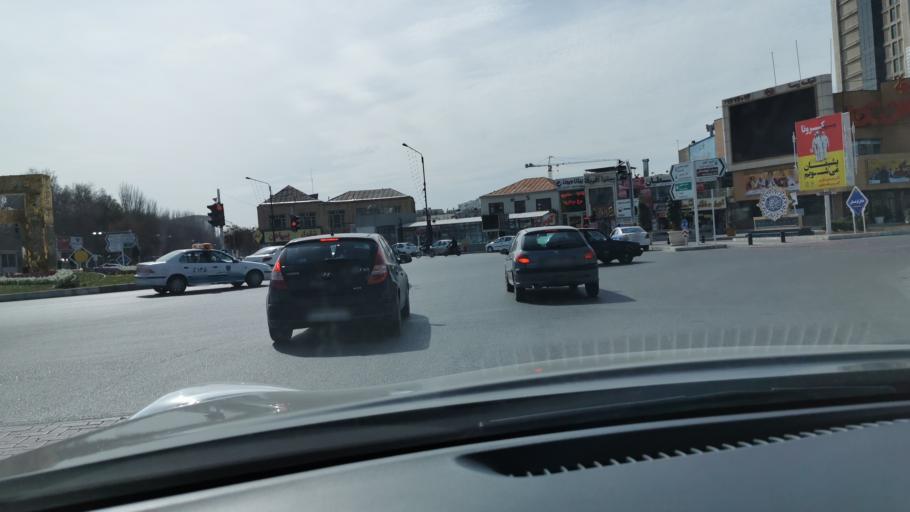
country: IR
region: Razavi Khorasan
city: Mashhad
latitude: 36.2914
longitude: 59.5856
